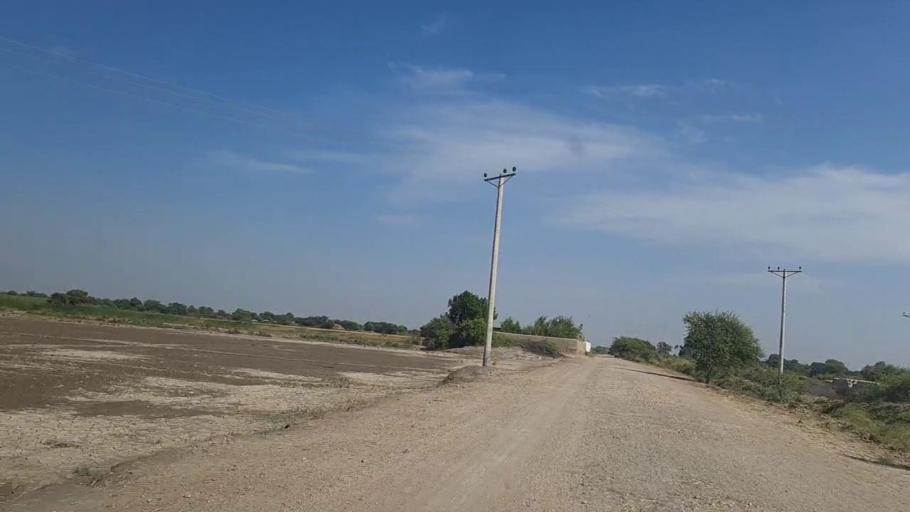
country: PK
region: Sindh
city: Bulri
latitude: 24.8646
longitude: 68.2626
